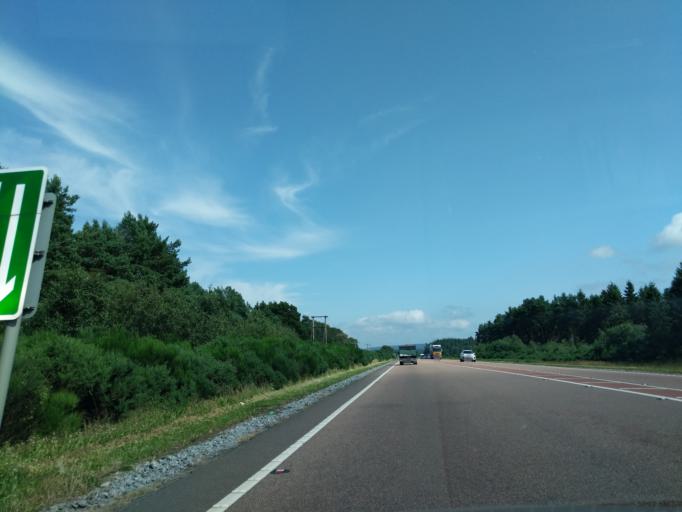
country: GB
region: Scotland
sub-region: Moray
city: Fochabers
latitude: 57.6232
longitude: -3.1321
